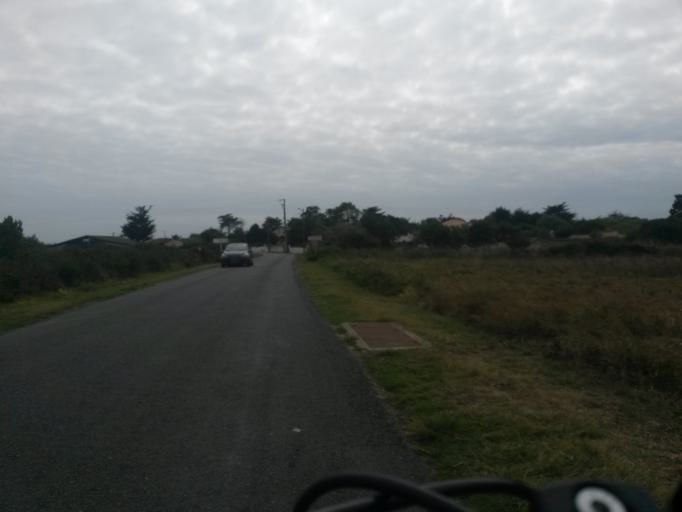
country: FR
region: Poitou-Charentes
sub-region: Departement de la Charente-Maritime
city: Saint-Denis-d'Oleron
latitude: 46.0180
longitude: -1.3921
